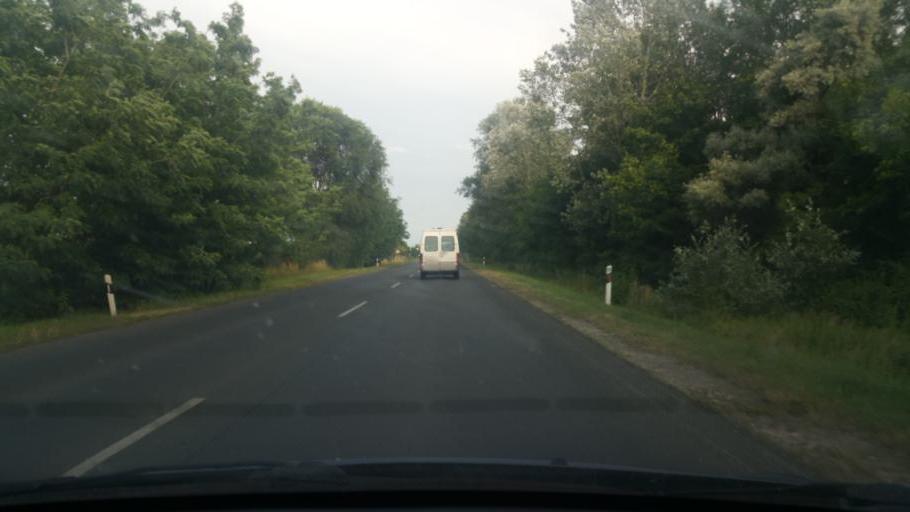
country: HU
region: Pest
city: Monor
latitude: 47.3394
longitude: 19.4308
